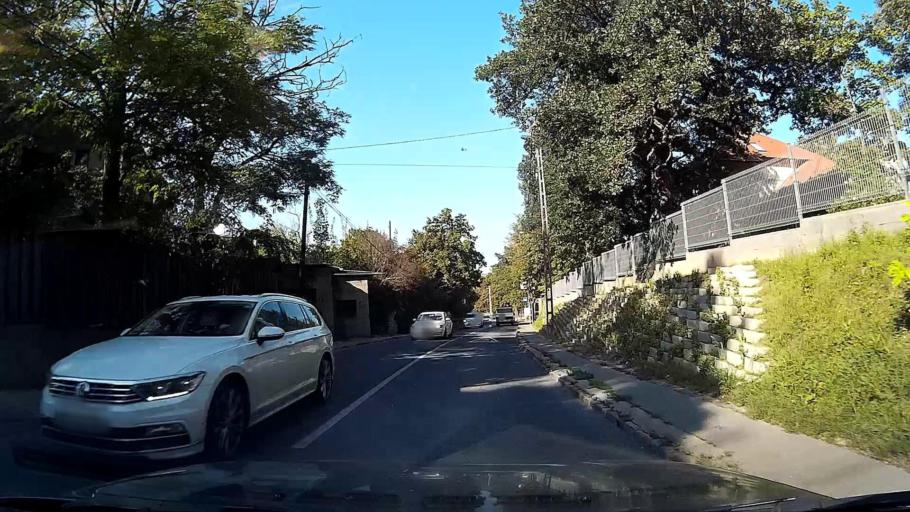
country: HU
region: Pest
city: Budaors
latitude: 47.4372
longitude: 18.9788
